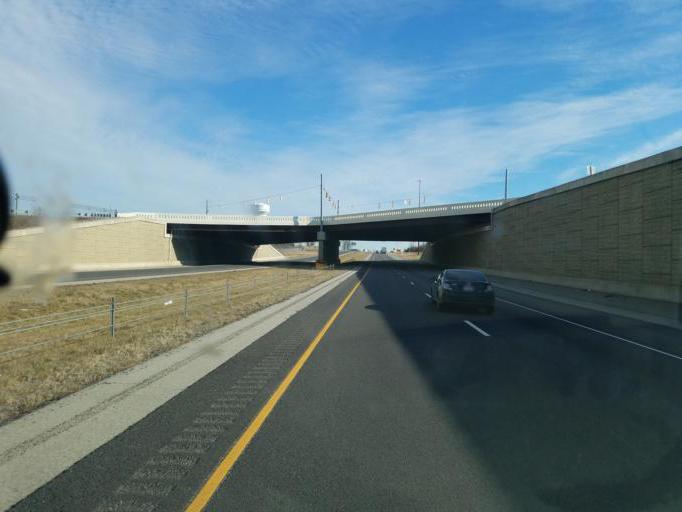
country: US
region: Indiana
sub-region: Wayne County
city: Richmond
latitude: 39.8720
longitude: -84.8899
